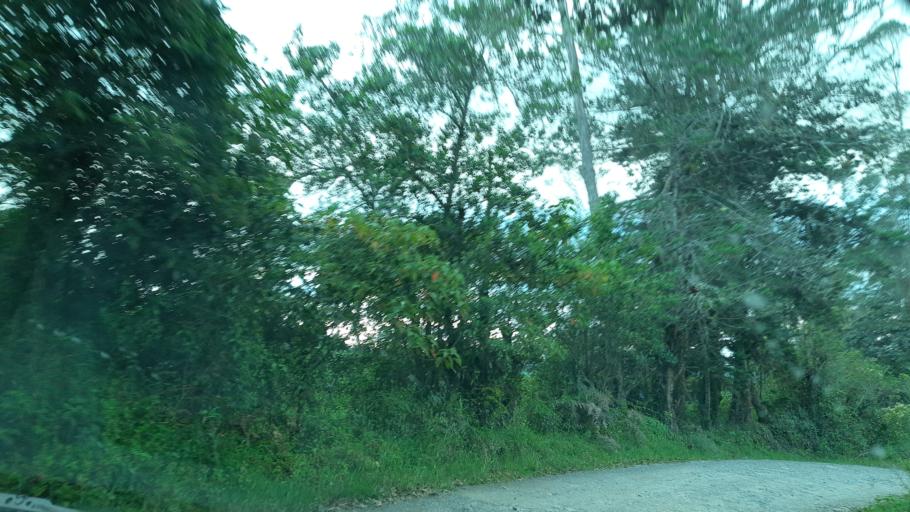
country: CO
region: Boyaca
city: Garagoa
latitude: 5.0823
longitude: -73.3220
